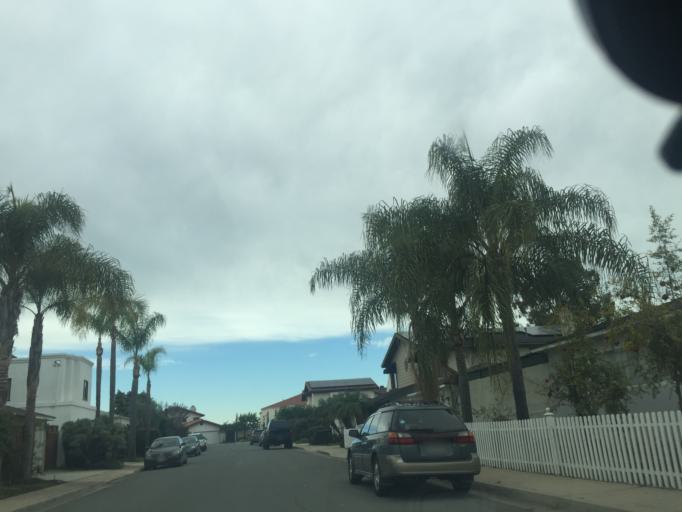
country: US
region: California
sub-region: San Diego County
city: Lemon Grove
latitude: 32.7681
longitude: -117.0936
